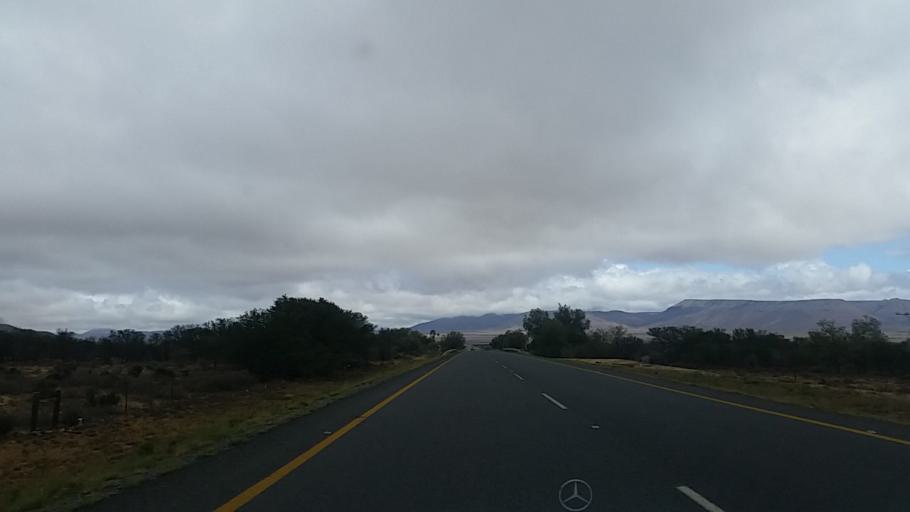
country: ZA
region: Eastern Cape
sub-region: Cacadu District Municipality
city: Graaff-Reinet
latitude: -31.9859
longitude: 24.6917
